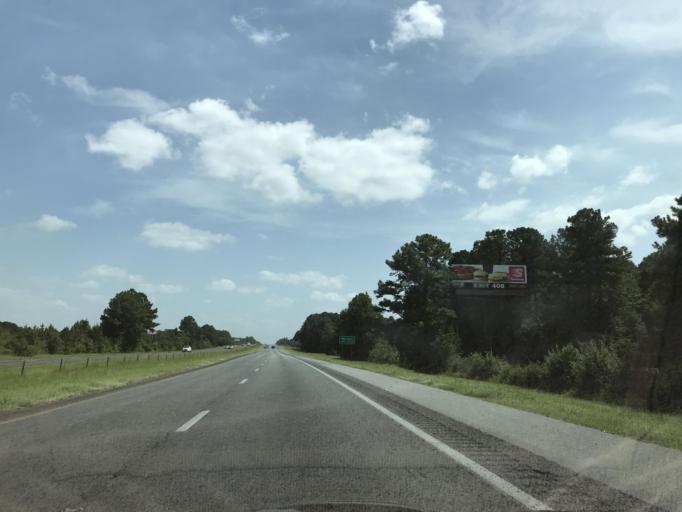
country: US
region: North Carolina
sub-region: Duplin County
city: Wallace
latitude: 34.7755
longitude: -77.9711
